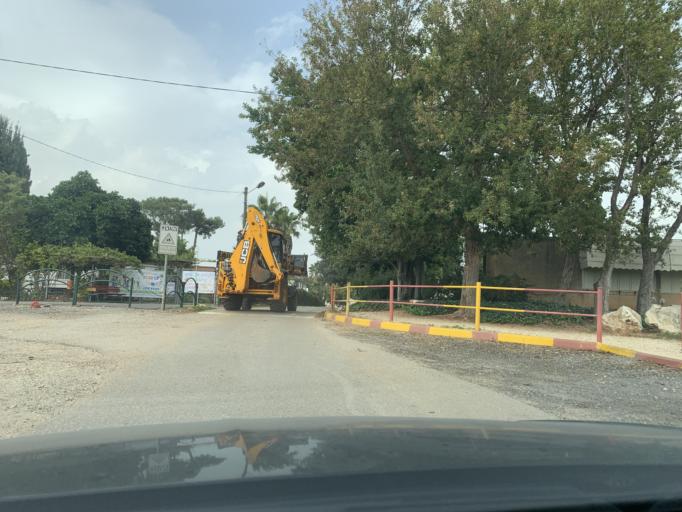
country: IL
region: Central District
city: Tirah
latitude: 32.2147
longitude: 34.9381
